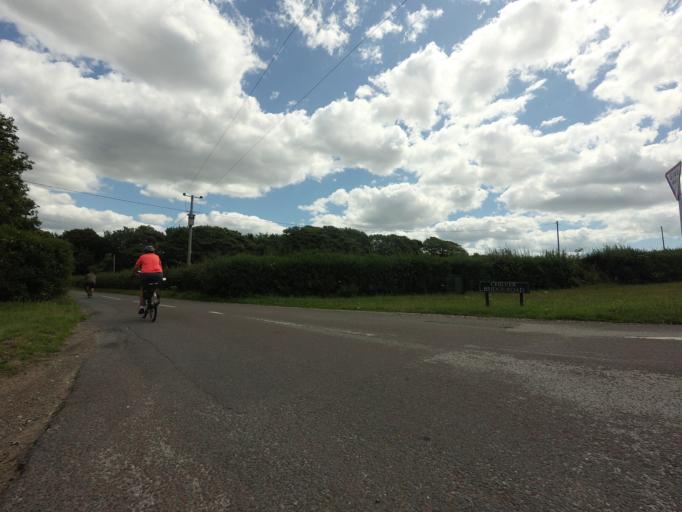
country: GB
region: England
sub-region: East Sussex
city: Seaford
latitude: 50.8373
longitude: 0.1655
